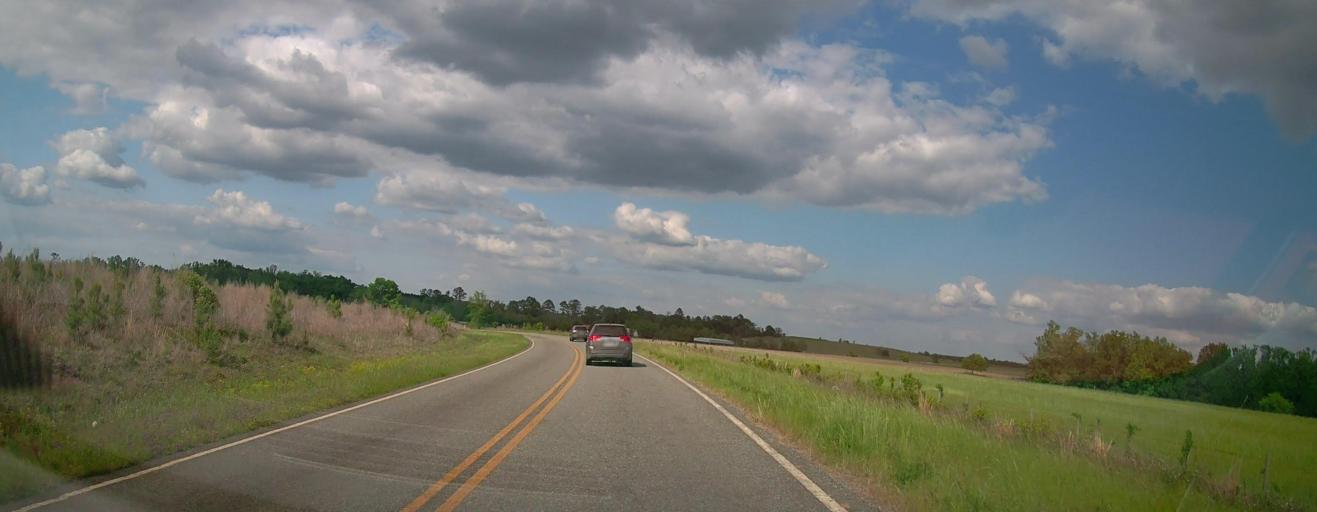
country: US
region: Georgia
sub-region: Laurens County
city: East Dublin
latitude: 32.7270
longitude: -82.9109
